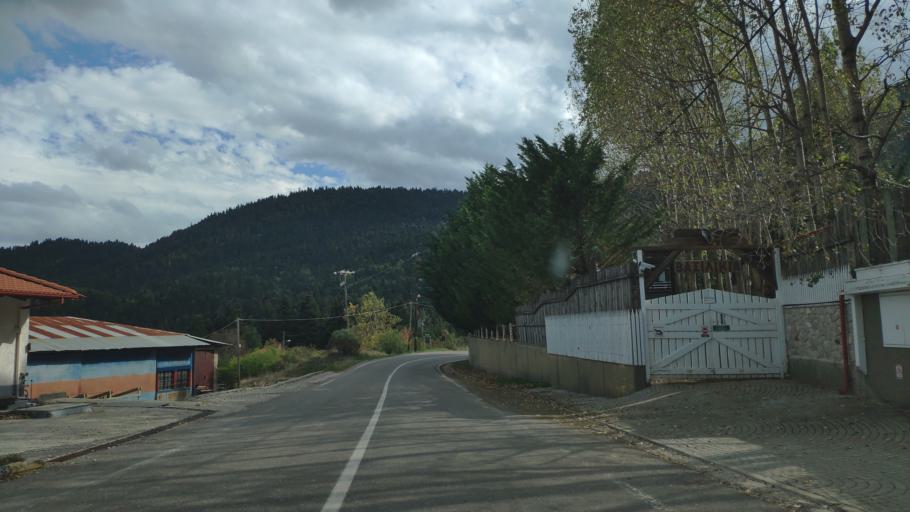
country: GR
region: Central Greece
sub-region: Nomos Fthiotidos
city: Stavros
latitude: 38.7344
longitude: 22.3473
